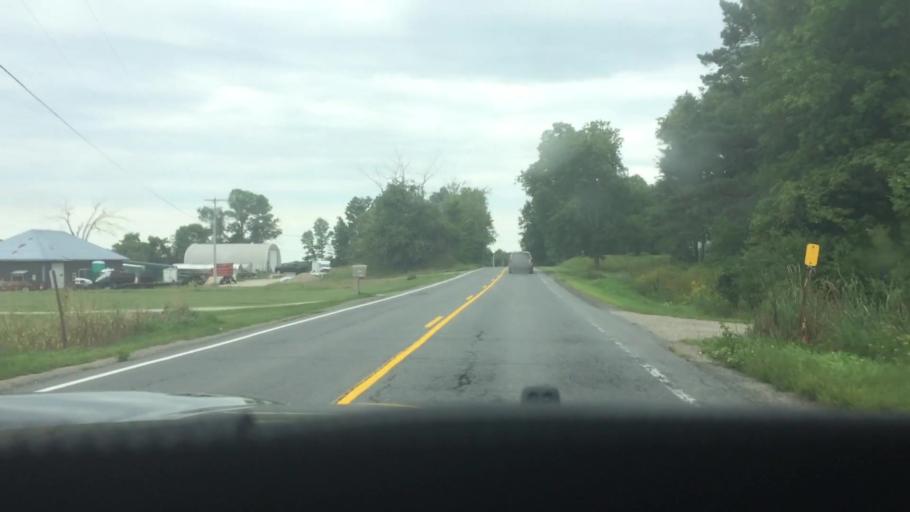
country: US
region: New York
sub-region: St. Lawrence County
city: Canton
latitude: 44.5492
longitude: -75.1448
